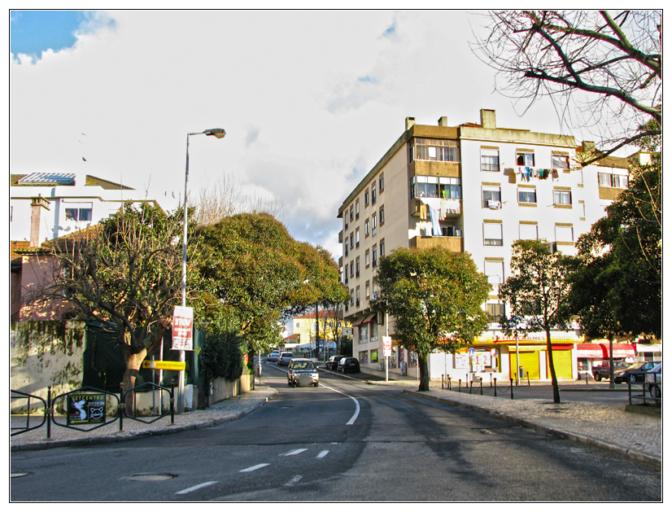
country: PT
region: Lisbon
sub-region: Sintra
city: Rio de Mouro
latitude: 38.7952
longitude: -9.3384
